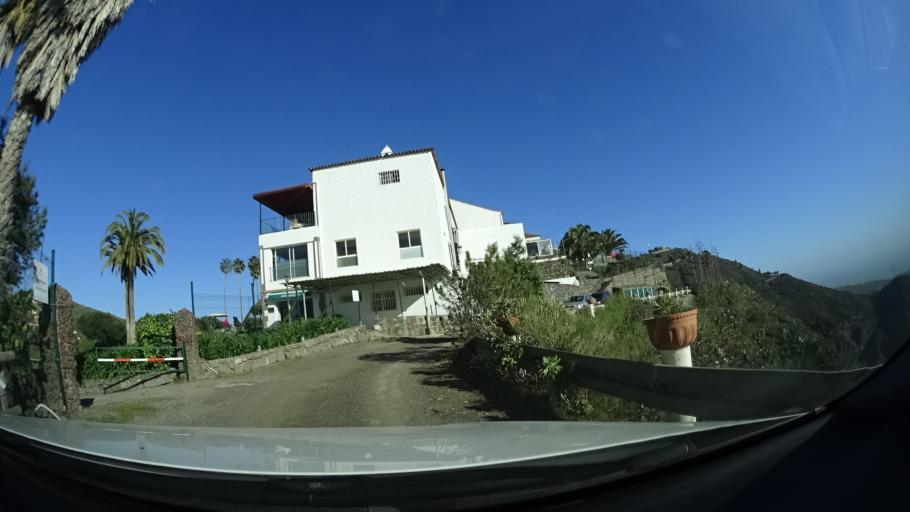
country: ES
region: Canary Islands
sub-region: Provincia de Las Palmas
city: Santa Brigida
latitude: 28.0307
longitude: -15.4598
